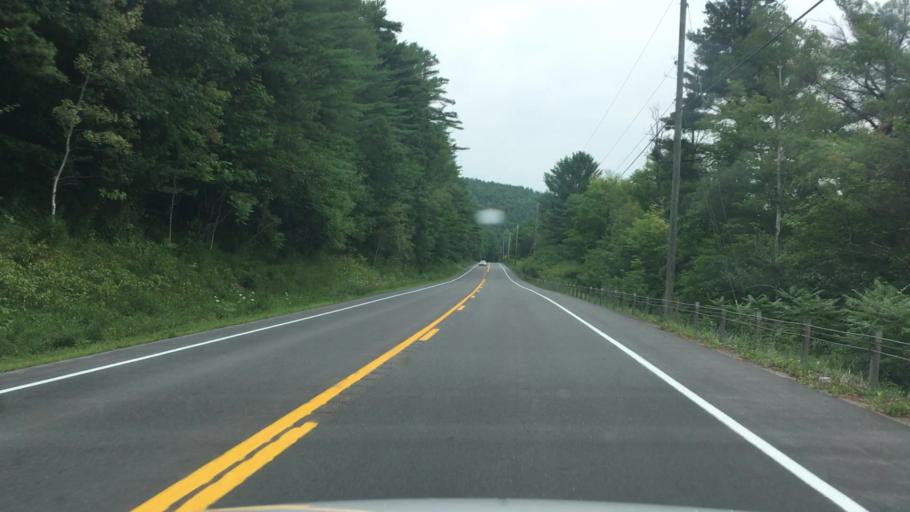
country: US
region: New York
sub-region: Essex County
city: Keeseville
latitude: 44.4703
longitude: -73.5712
